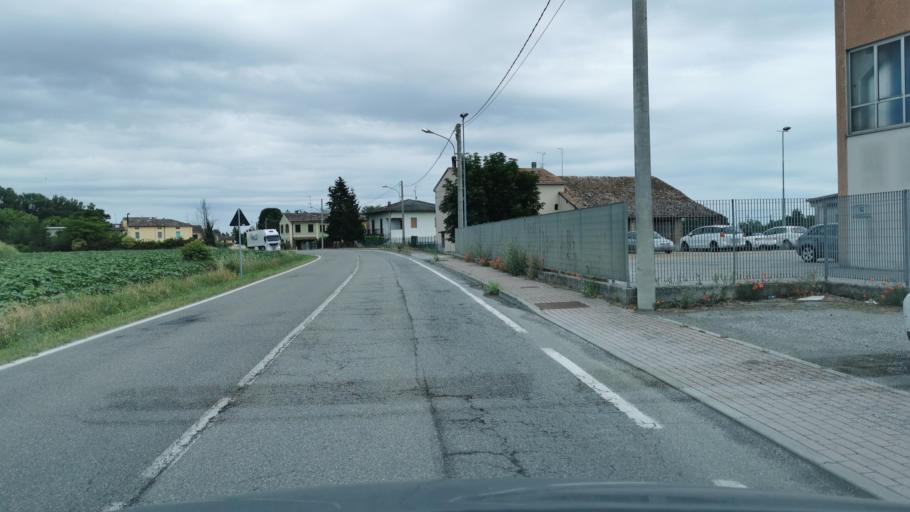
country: IT
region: Emilia-Romagna
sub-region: Provincia di Parma
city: Soragna
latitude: 44.9046
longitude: 10.0963
